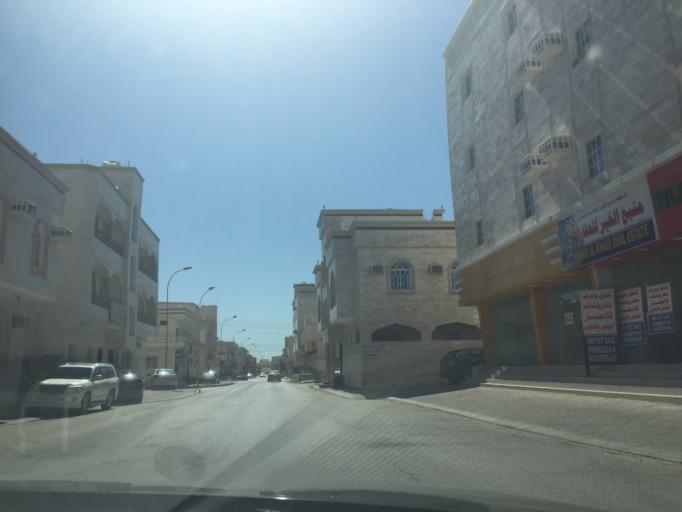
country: OM
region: Zufar
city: Salalah
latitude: 17.0253
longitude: 54.1565
